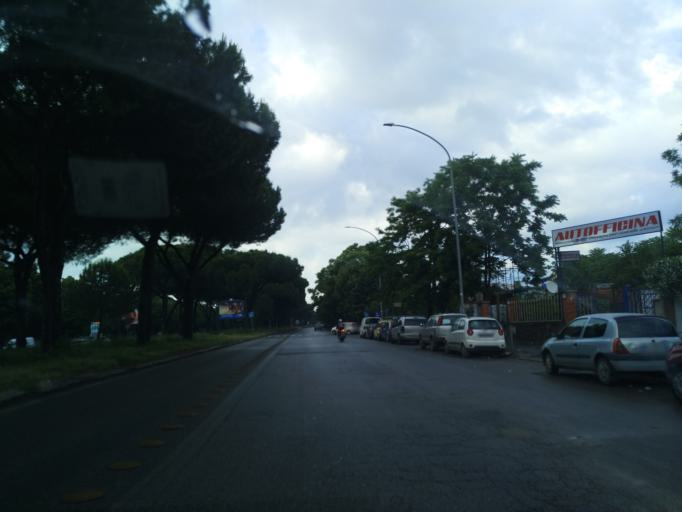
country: IT
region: Latium
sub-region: Citta metropolitana di Roma Capitale
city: Rome
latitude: 41.8840
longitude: 12.5735
